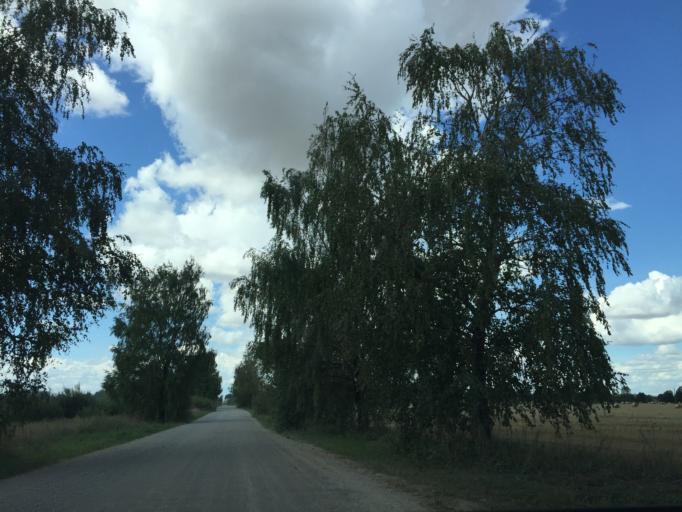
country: LV
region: Rundales
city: Pilsrundale
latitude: 56.2999
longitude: 23.9990
